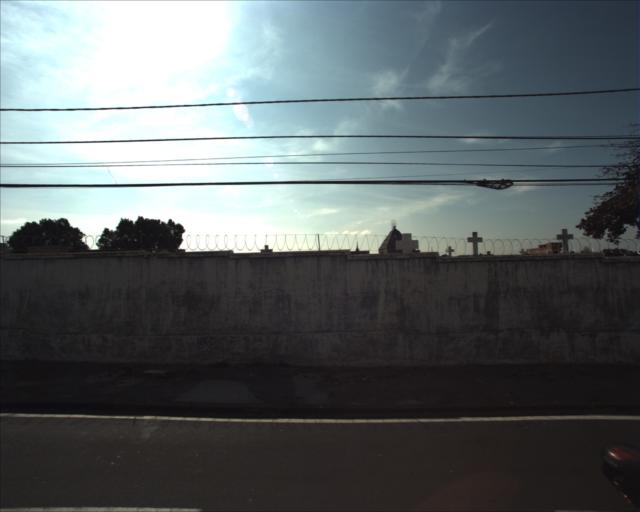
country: BR
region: Sao Paulo
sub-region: Sorocaba
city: Sorocaba
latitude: -23.4899
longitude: -47.4624
